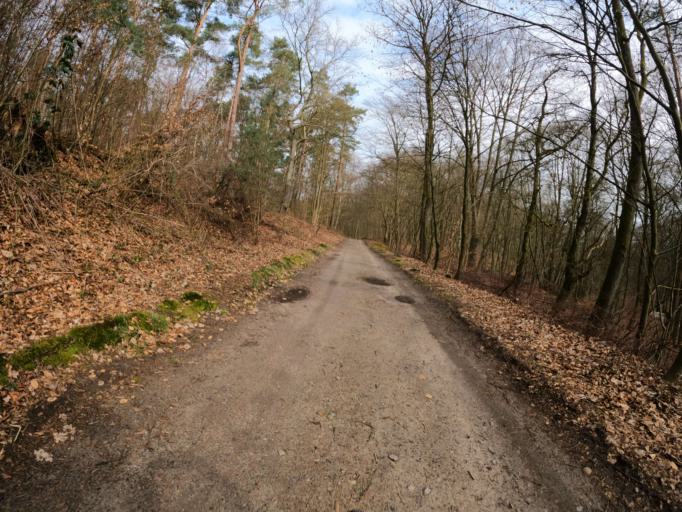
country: DE
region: Hamburg
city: Harburg
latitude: 53.4647
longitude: 9.9338
